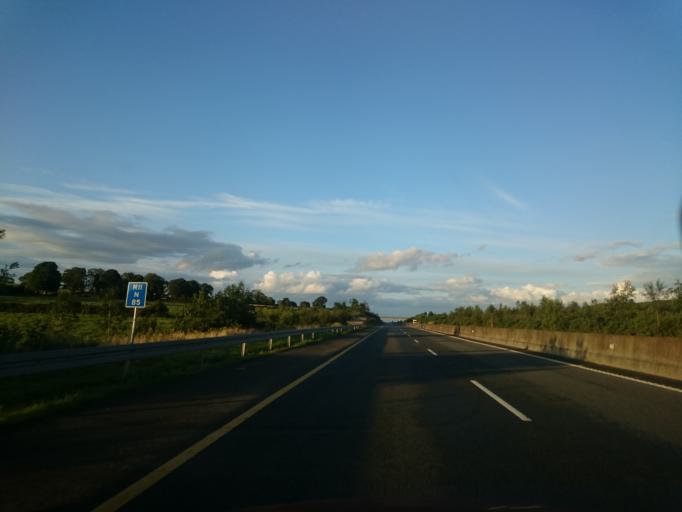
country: IE
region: Leinster
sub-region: Loch Garman
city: Gorey
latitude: 52.6466
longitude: -6.3276
